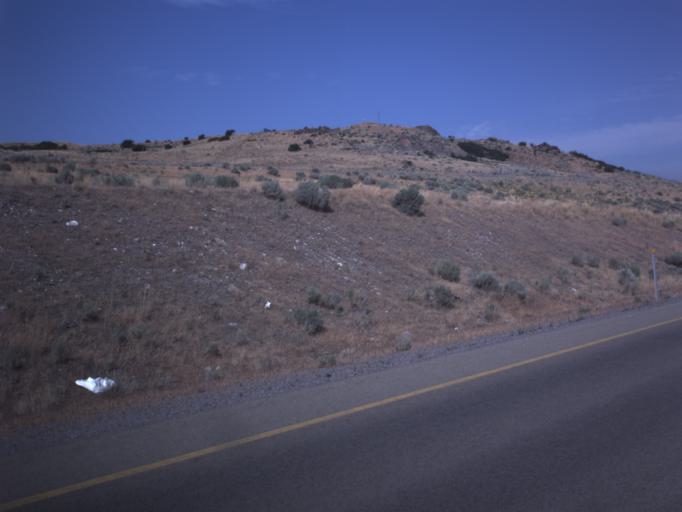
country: US
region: Utah
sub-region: Salt Lake County
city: Bluffdale
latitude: 40.4693
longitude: -111.9642
